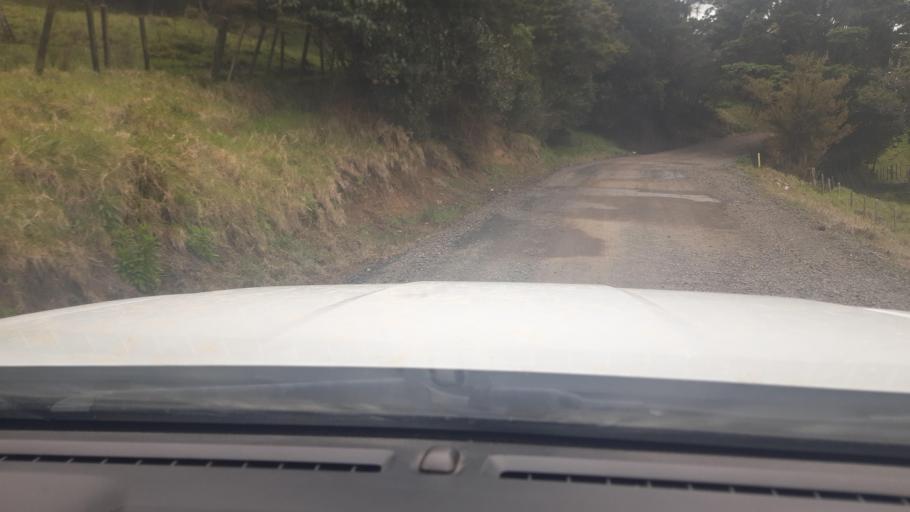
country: NZ
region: Northland
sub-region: Far North District
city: Kaitaia
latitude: -35.0806
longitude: 173.3213
